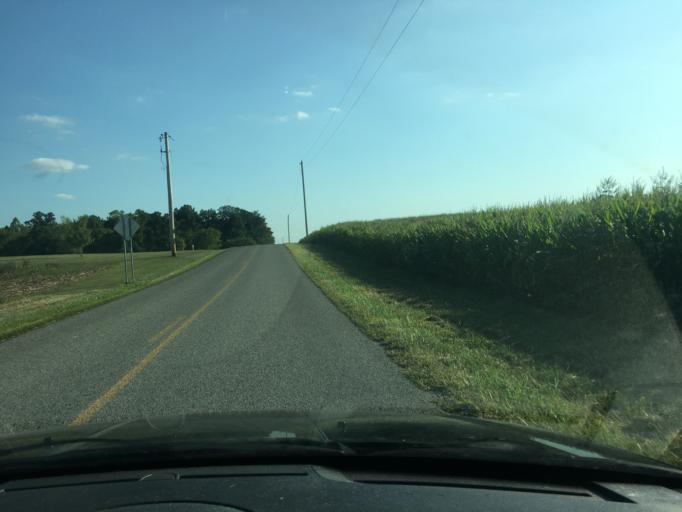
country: US
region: Ohio
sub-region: Logan County
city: West Liberty
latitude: 40.2741
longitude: -83.8017
